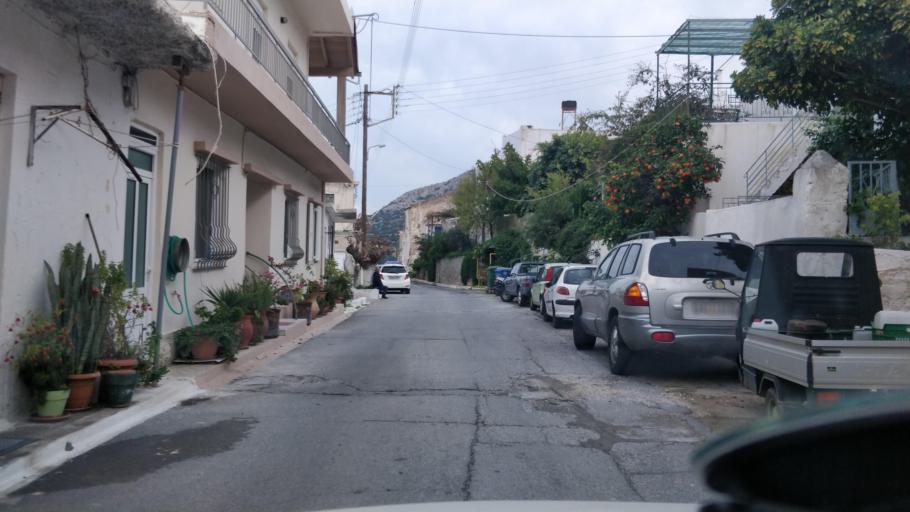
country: GR
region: Crete
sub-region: Nomos Lasithiou
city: Agios Nikolaos
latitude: 35.1151
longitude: 25.7230
